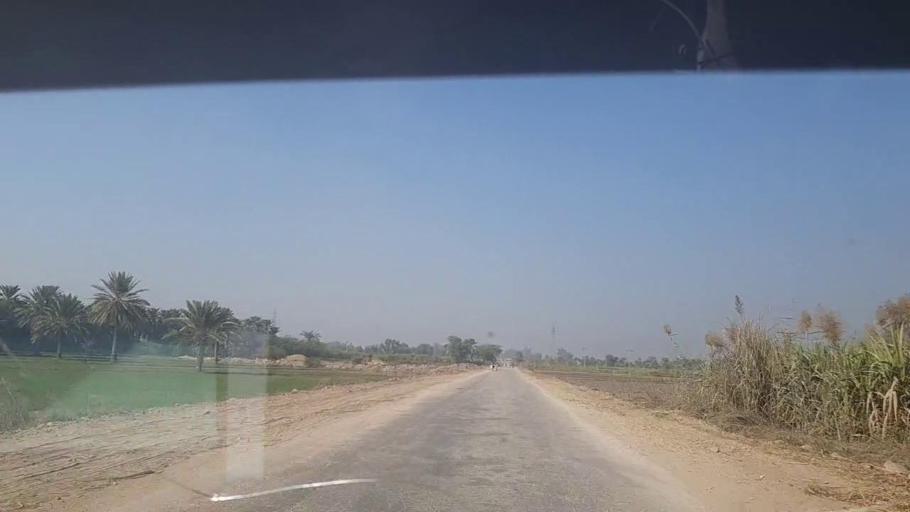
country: PK
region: Sindh
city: Kot Diji
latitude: 27.4250
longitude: 68.6573
